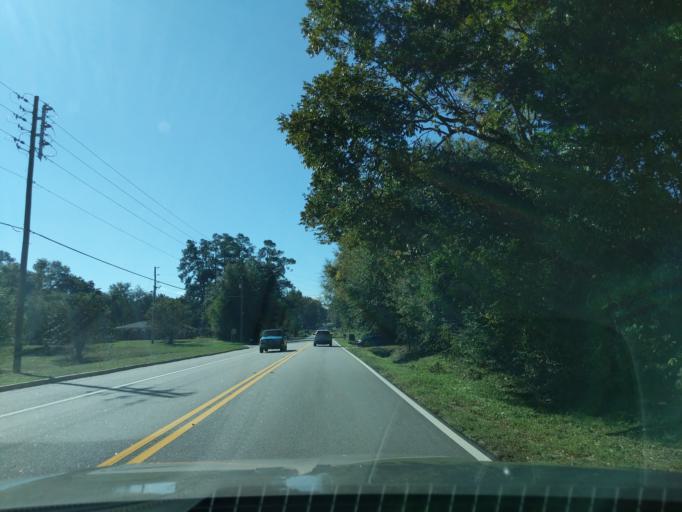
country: US
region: Georgia
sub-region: Richmond County
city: Hephzibah
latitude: 33.3381
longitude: -82.0069
